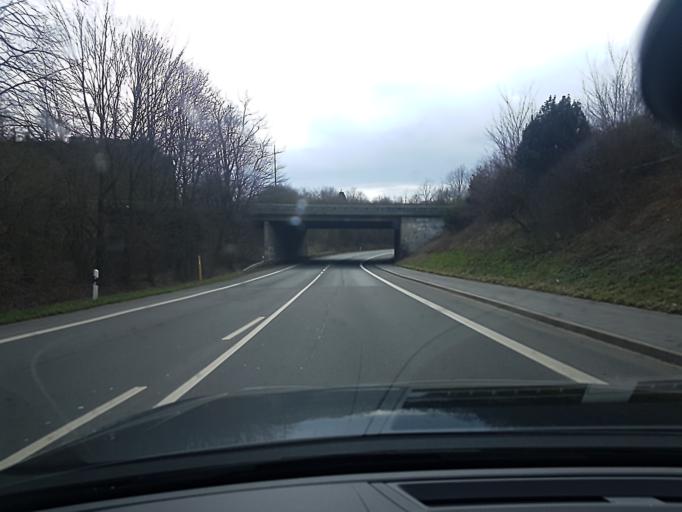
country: DE
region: North Rhine-Westphalia
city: Iserlohn
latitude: 51.3832
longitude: 7.6725
